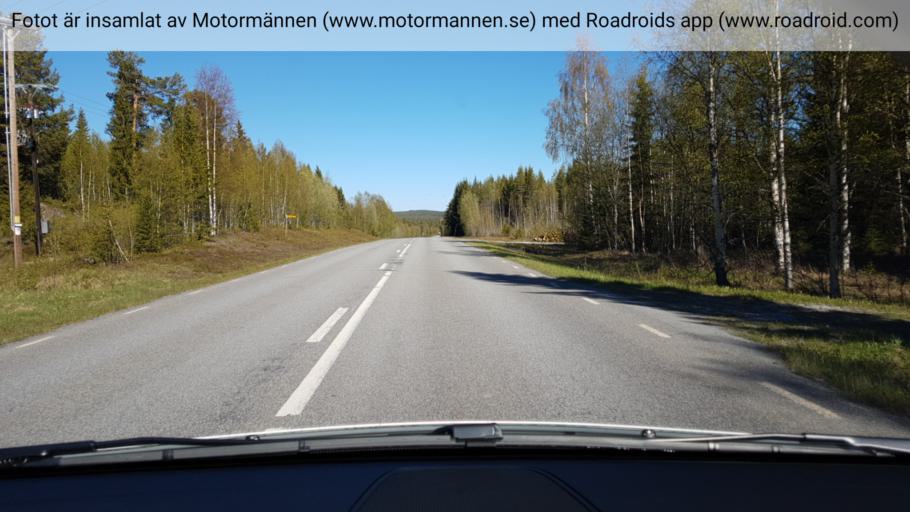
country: SE
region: Jaemtland
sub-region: Stroemsunds Kommun
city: Stroemsund
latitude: 64.3077
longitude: 15.2437
